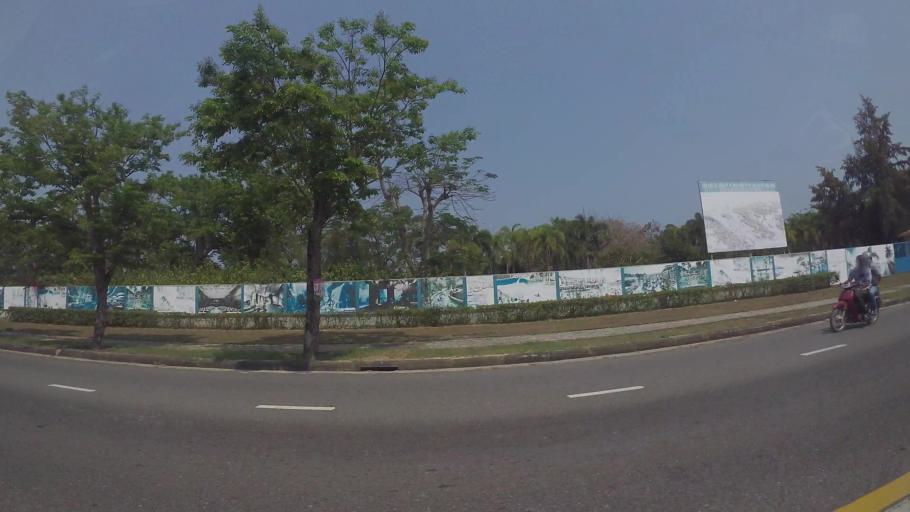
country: VN
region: Da Nang
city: Ngu Hanh Son
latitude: 15.9892
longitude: 108.2711
